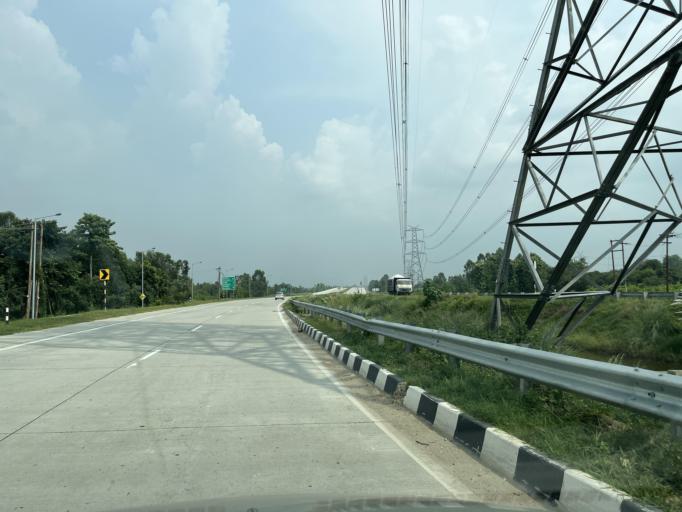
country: IN
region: Uttarakhand
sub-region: Udham Singh Nagar
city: Jaspur
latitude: 29.2981
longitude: 78.8360
